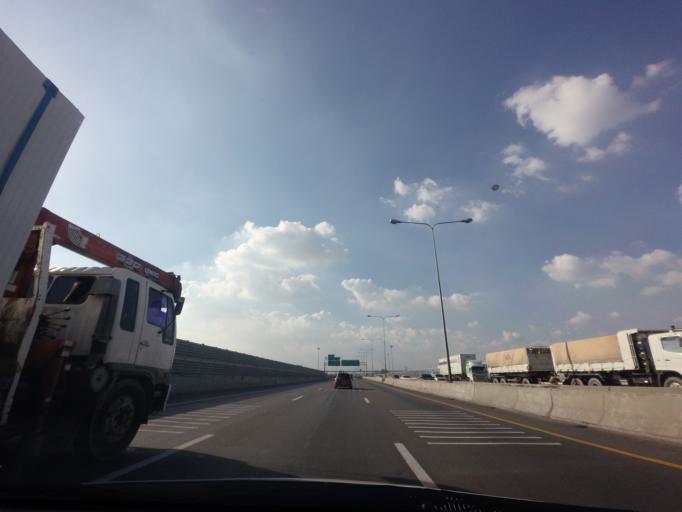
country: TH
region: Samut Prakan
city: Samut Prakan
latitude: 13.6253
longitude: 100.5976
